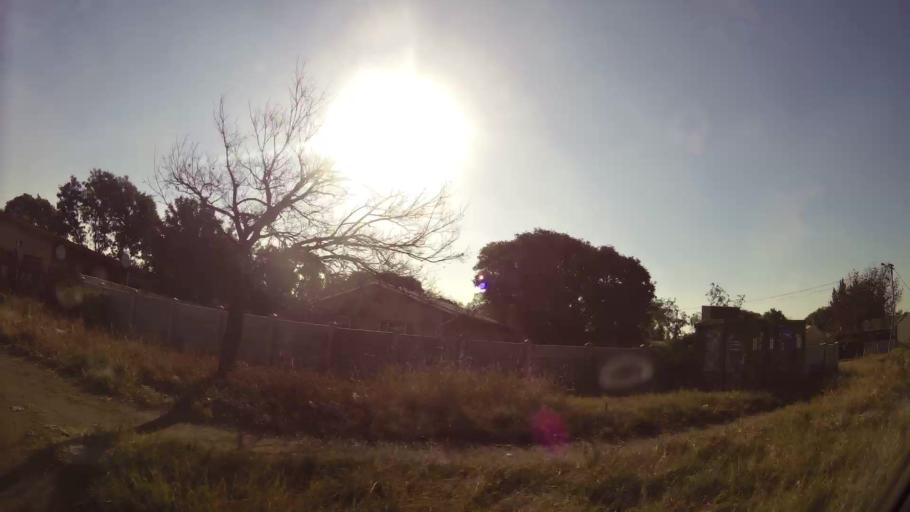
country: ZA
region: North-West
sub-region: Bojanala Platinum District Municipality
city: Rustenburg
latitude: -25.6614
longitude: 27.2645
